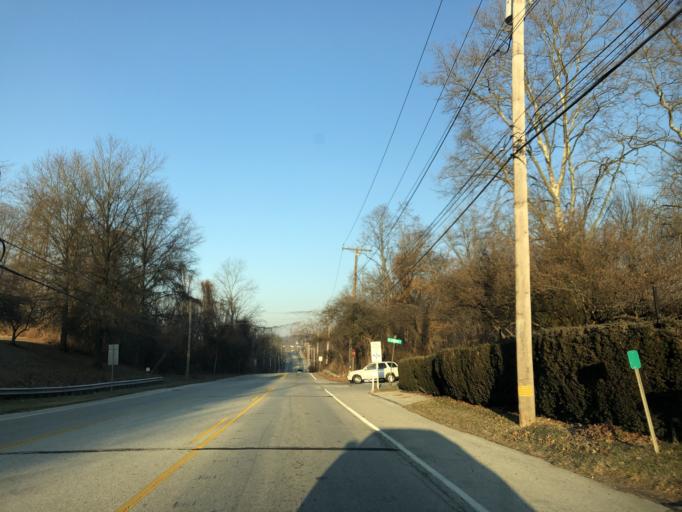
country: US
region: Pennsylvania
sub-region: Chester County
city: West Chester
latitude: 39.9616
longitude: -75.6219
